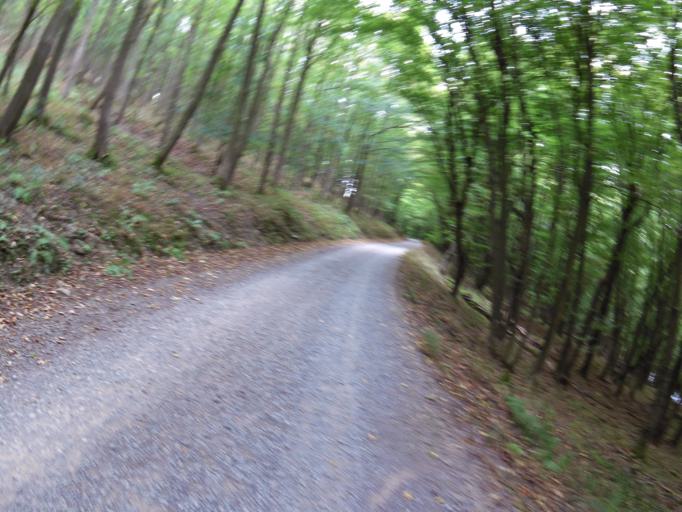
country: DE
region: North Rhine-Westphalia
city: Heimbach
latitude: 50.6070
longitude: 6.4208
